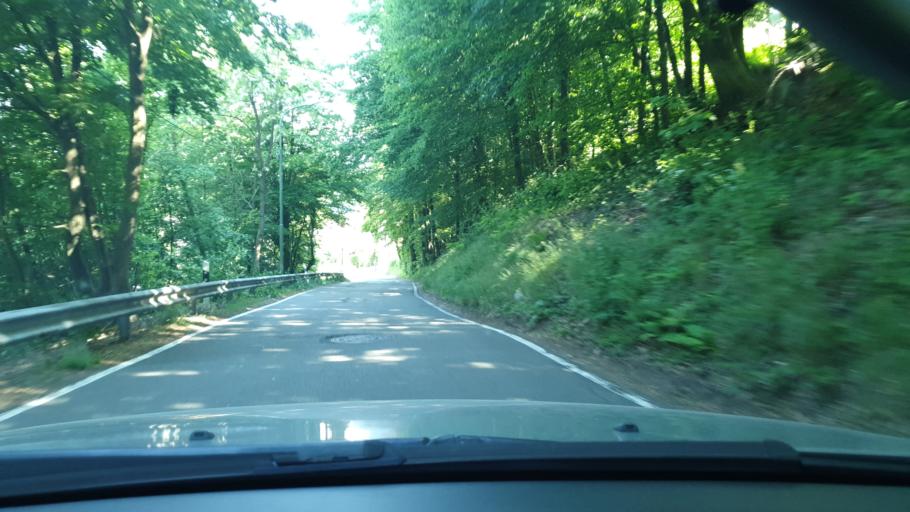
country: DE
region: Rheinland-Pfalz
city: Otterberg
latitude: 49.4758
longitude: 7.7873
